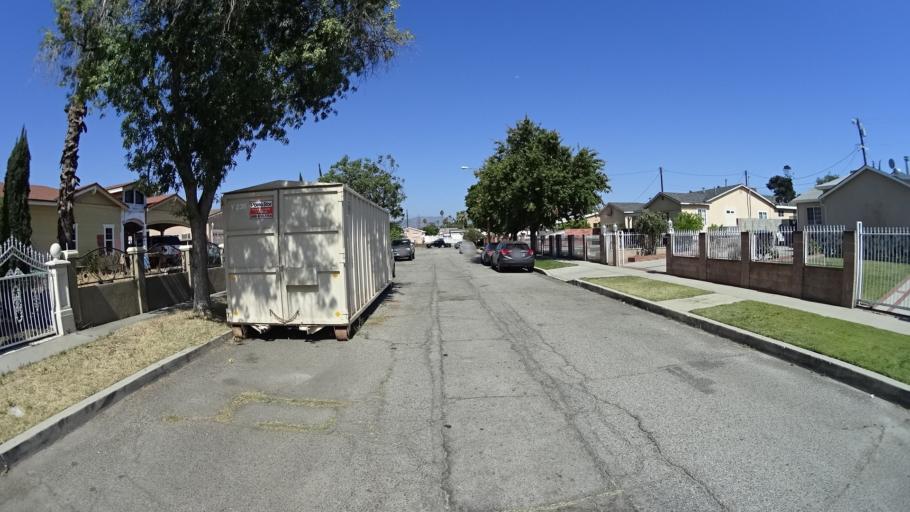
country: US
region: California
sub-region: Los Angeles County
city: Van Nuys
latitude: 34.2174
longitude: -118.4173
